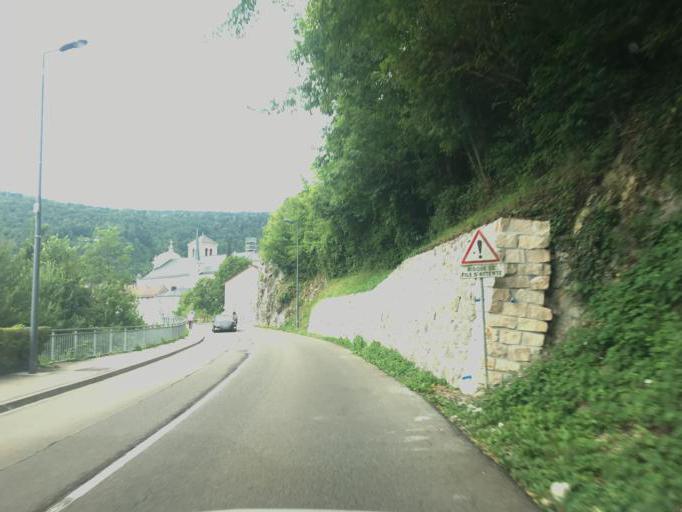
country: FR
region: Franche-Comte
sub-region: Departement du Jura
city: Saint-Claude
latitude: 46.3848
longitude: 5.8693
